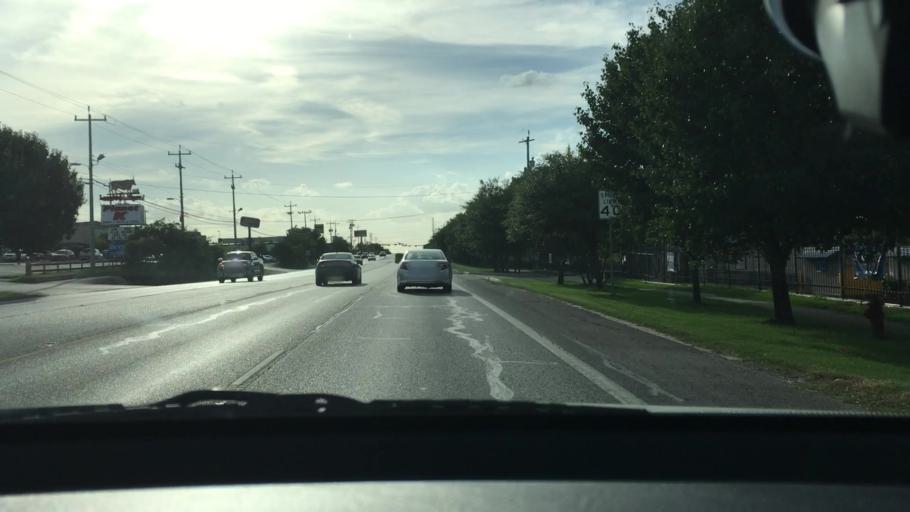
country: US
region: Texas
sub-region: Bexar County
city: Live Oak
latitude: 29.5564
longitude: -98.3169
